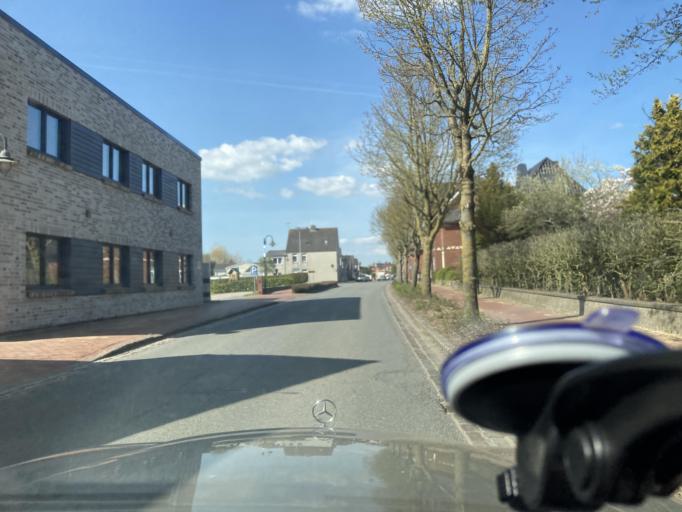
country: DE
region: Schleswig-Holstein
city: Lehe
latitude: 54.3273
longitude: 9.0234
